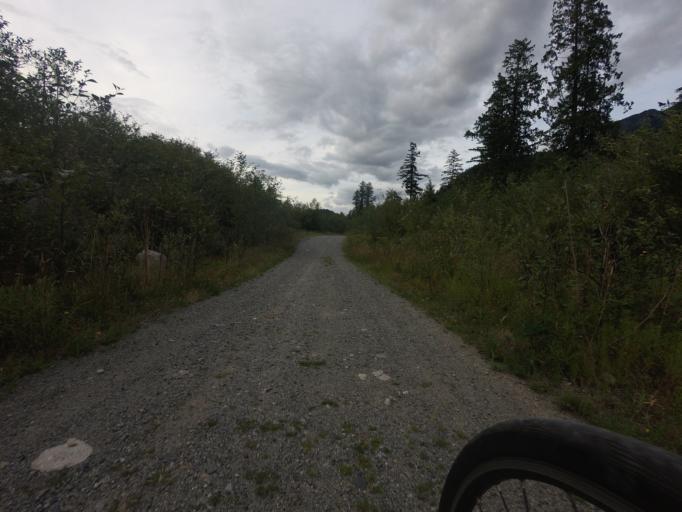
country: CA
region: British Columbia
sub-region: Greater Vancouver Regional District
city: Lions Bay
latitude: 49.5802
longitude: -123.2268
